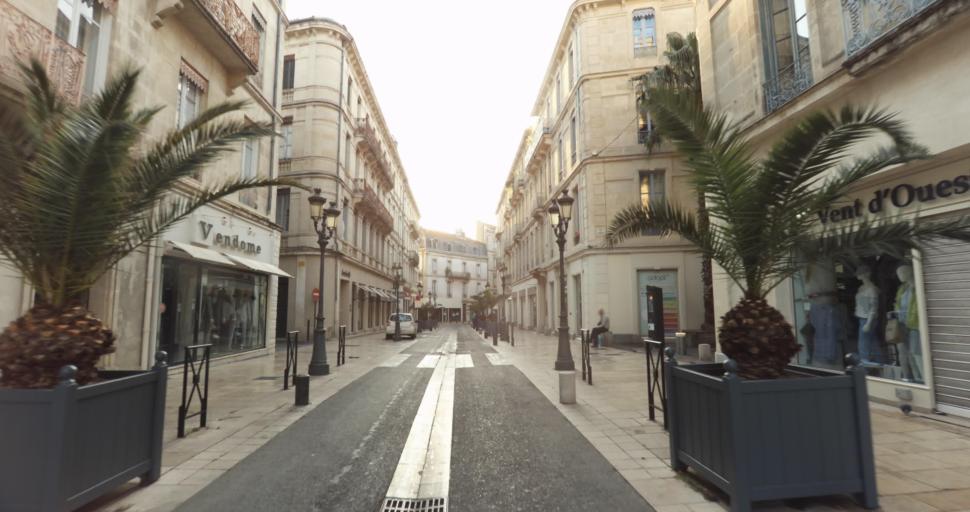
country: FR
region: Languedoc-Roussillon
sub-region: Departement du Gard
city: Nimes
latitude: 43.8390
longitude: 4.3597
